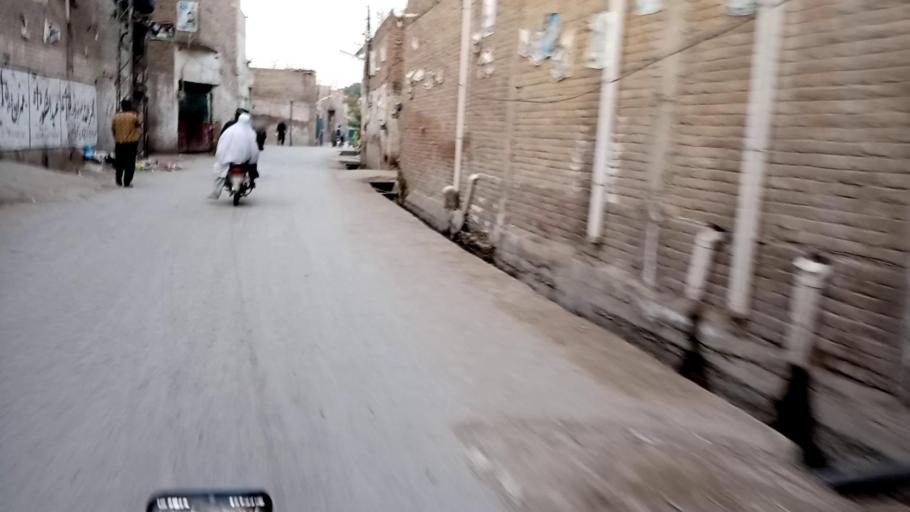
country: PK
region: Khyber Pakhtunkhwa
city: Peshawar
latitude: 34.0290
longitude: 71.4889
